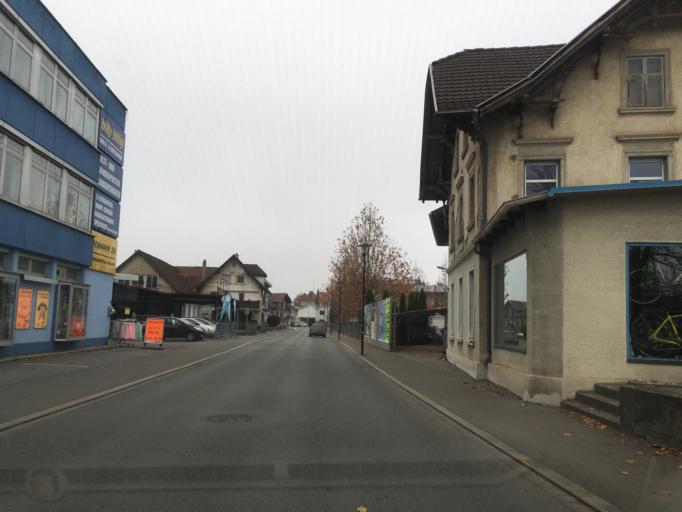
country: AT
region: Vorarlberg
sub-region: Politischer Bezirk Dornbirn
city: Lustenau
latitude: 47.4305
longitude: 9.6600
